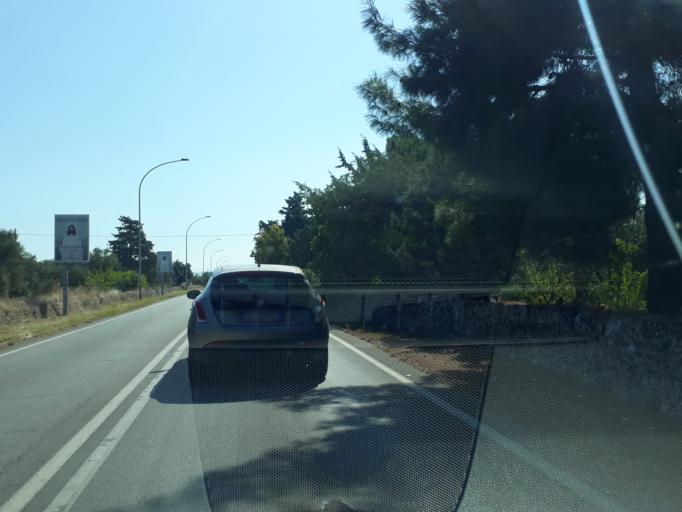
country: IT
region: Apulia
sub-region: Provincia di Bari
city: Monopoli
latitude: 40.9302
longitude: 17.3121
